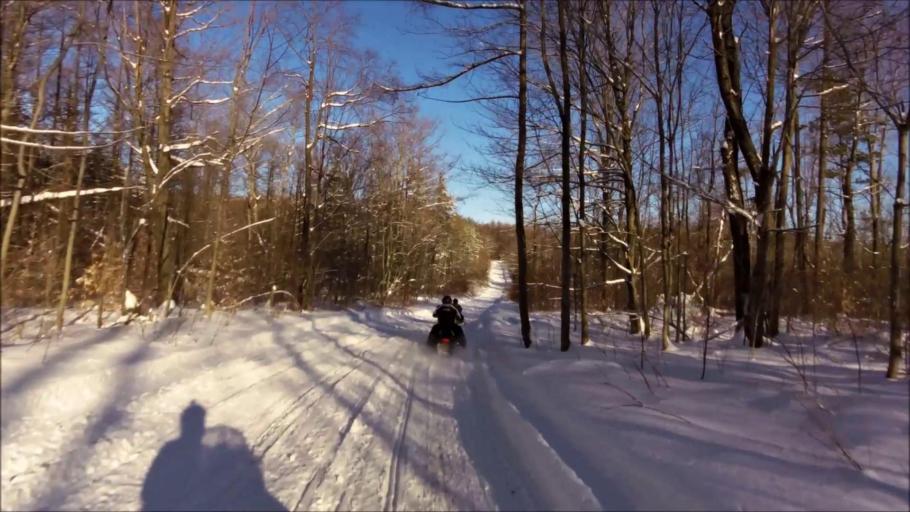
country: US
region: New York
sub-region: Chautauqua County
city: Mayville
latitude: 42.2800
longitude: -79.4013
